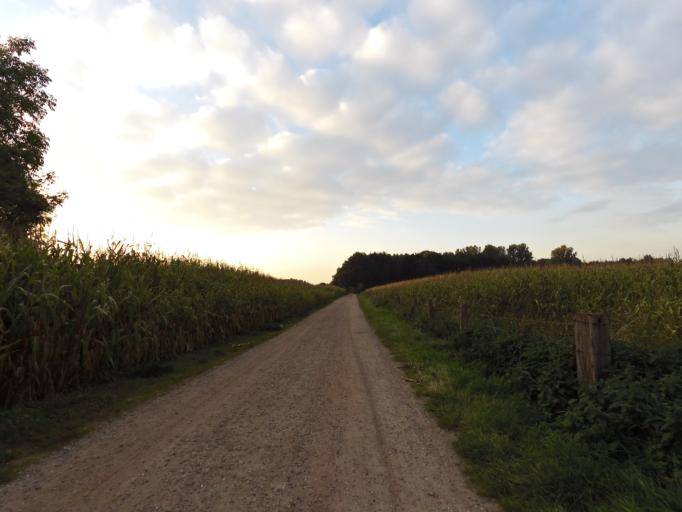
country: NL
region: Gelderland
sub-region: Gemeente Doesburg
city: Doesburg
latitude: 51.9537
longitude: 6.1991
